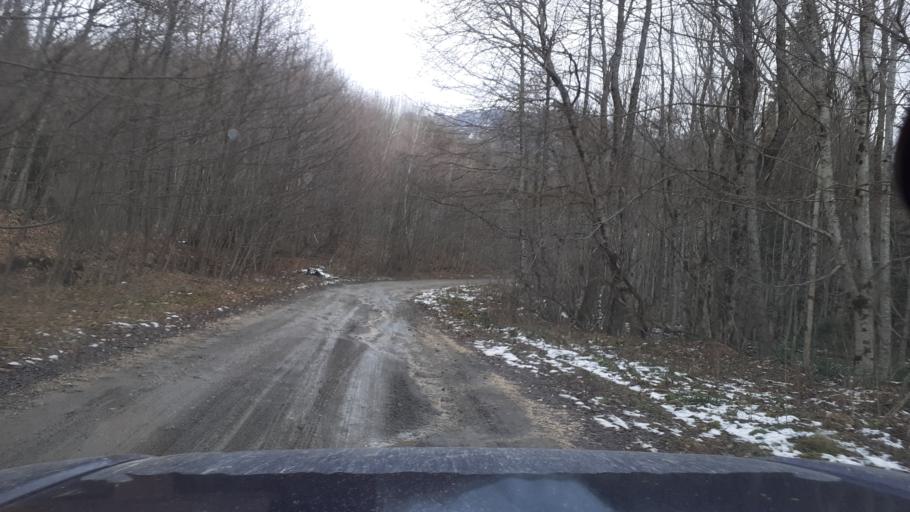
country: RU
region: Krasnodarskiy
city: Neftegorsk
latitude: 44.0807
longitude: 39.7375
